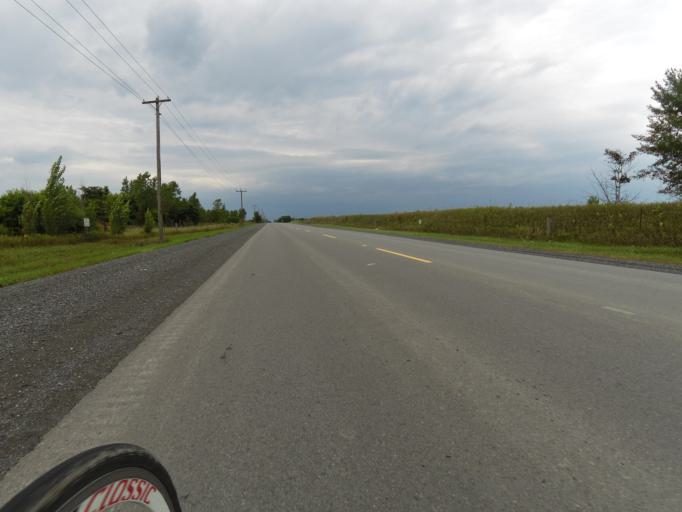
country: CA
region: Ontario
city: Bells Corners
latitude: 45.2296
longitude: -75.7796
